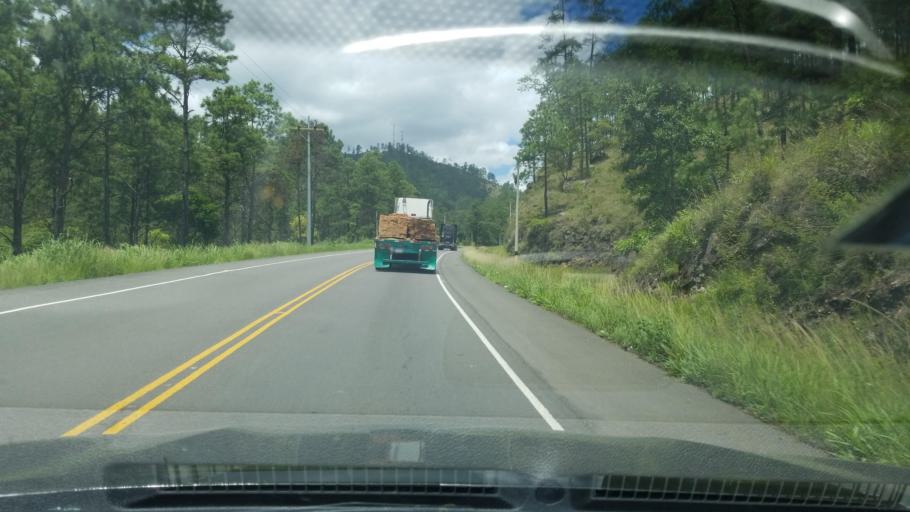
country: HN
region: Francisco Morazan
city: Talanga
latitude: 14.3999
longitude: -87.1253
